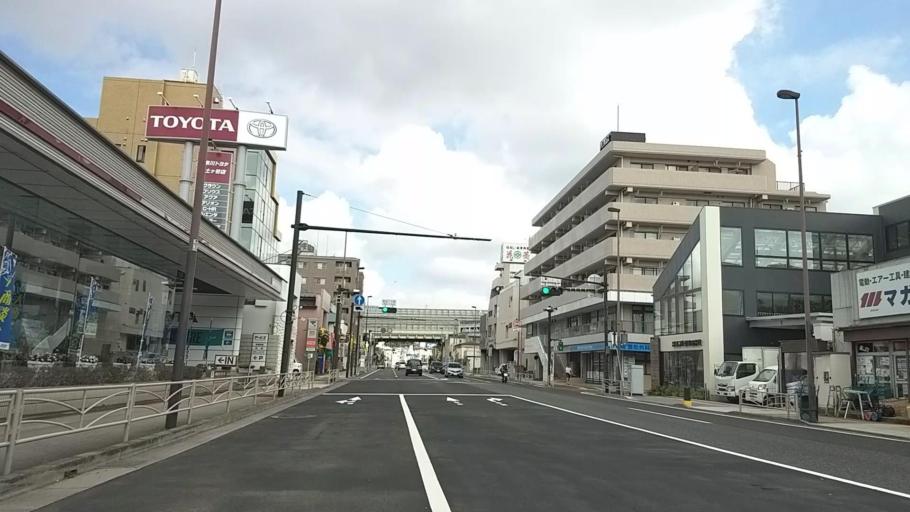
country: JP
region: Kanagawa
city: Yokohama
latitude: 35.4632
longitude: 139.5927
